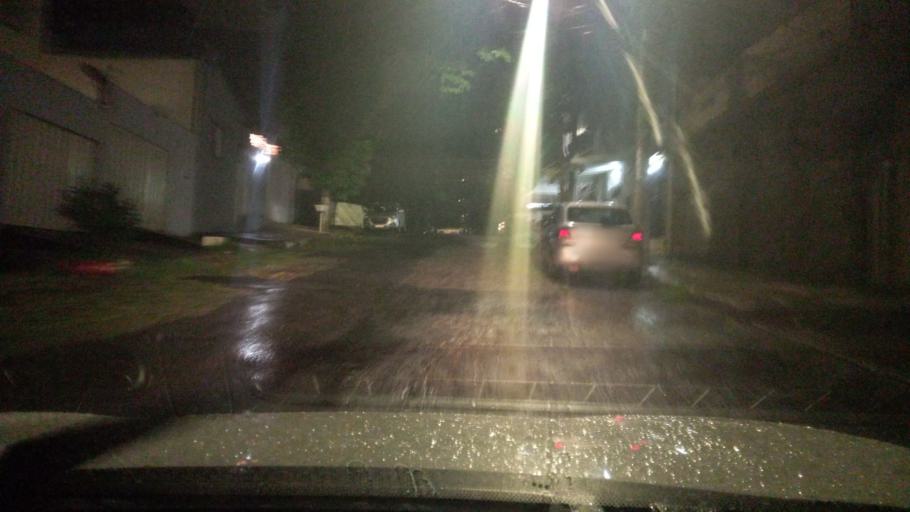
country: BR
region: Minas Gerais
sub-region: Belo Horizonte
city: Belo Horizonte
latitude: -19.9117
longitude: -43.9107
